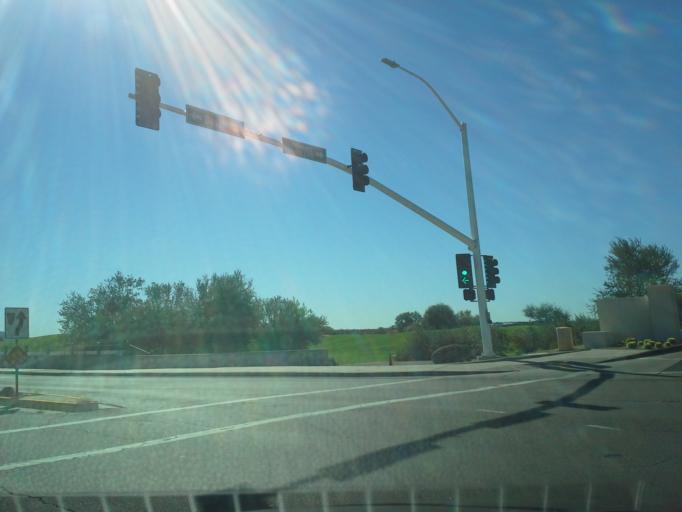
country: US
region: Arizona
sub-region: Maricopa County
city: Paradise Valley
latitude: 33.6402
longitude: -111.9074
